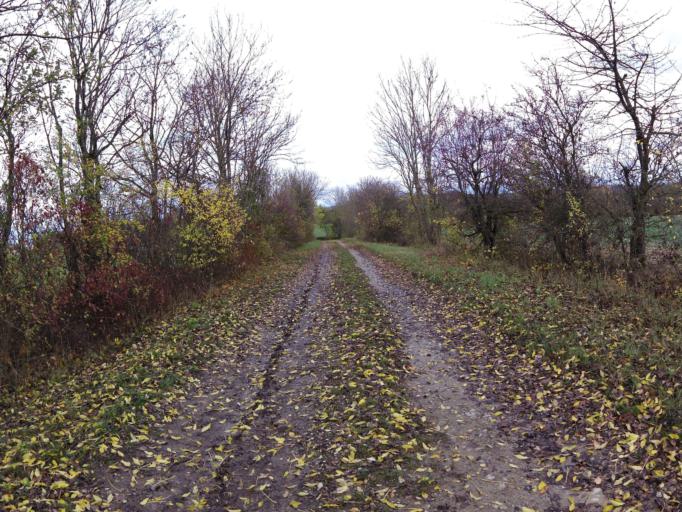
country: DE
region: Thuringia
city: Ifta
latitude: 51.0585
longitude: 10.1324
